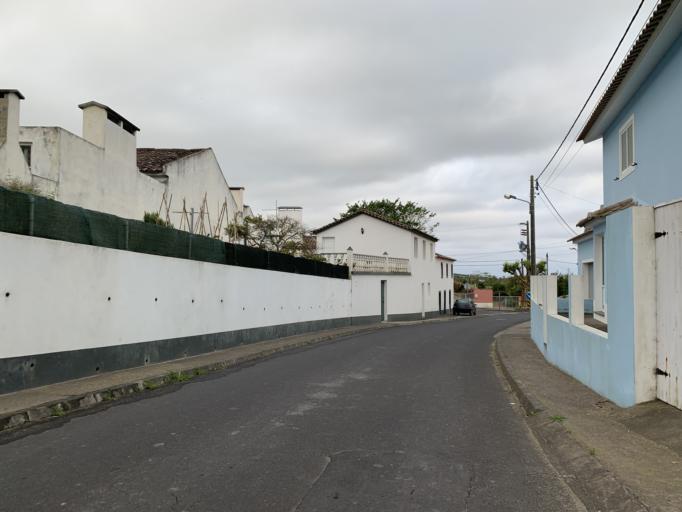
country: PT
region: Azores
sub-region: Ponta Delgada
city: Arrifes
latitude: 37.8477
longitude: -25.8402
